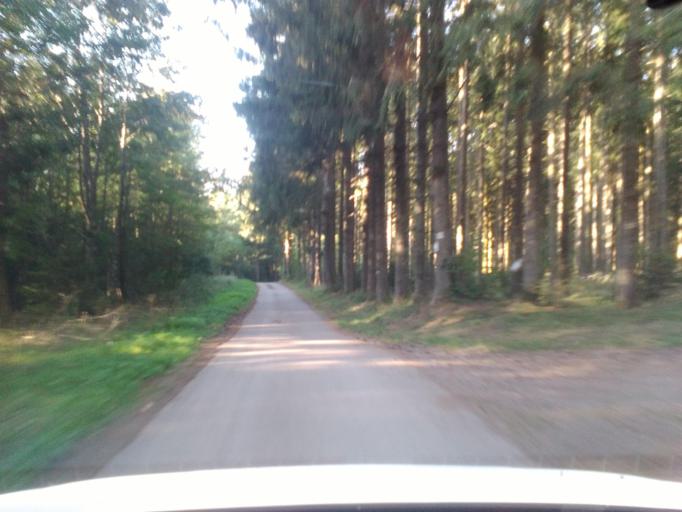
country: FR
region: Lorraine
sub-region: Departement des Vosges
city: Senones
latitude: 48.3409
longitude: 7.0542
